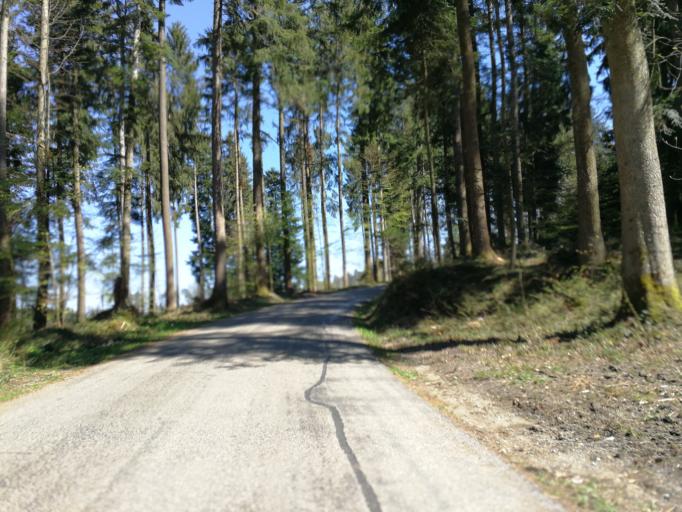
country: CH
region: Zurich
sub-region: Bezirk Uster
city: Aesch
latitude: 47.3076
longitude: 8.6558
